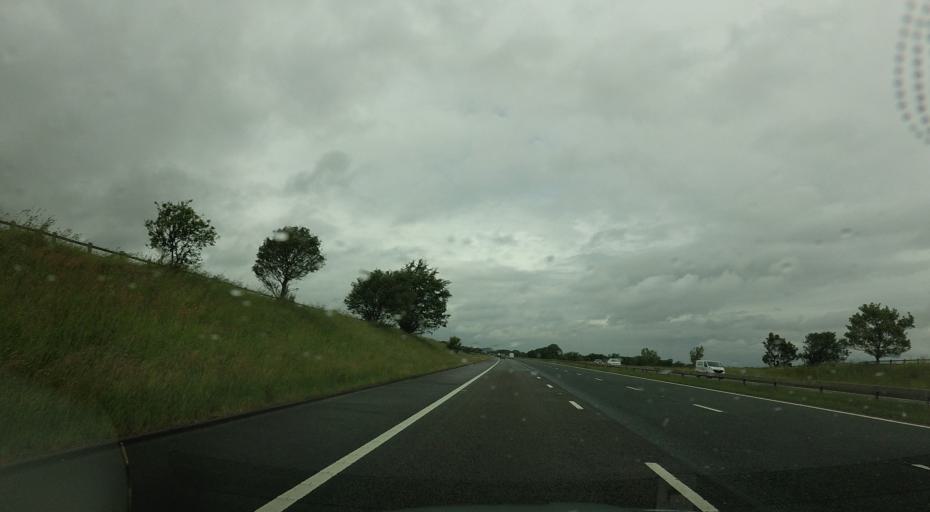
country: GB
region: England
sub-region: Cumbria
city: Scotby
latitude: 54.7837
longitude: -2.8582
